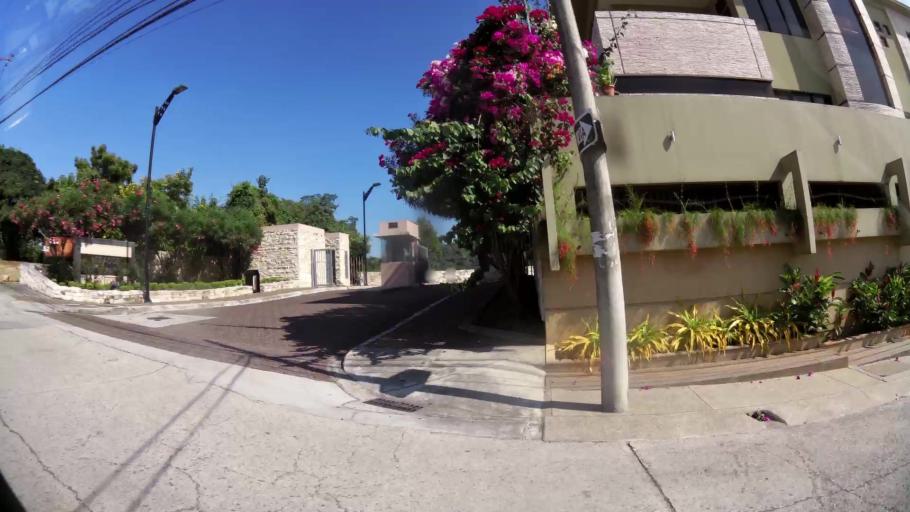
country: EC
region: Guayas
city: Guayaquil
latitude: -2.1796
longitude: -79.9143
